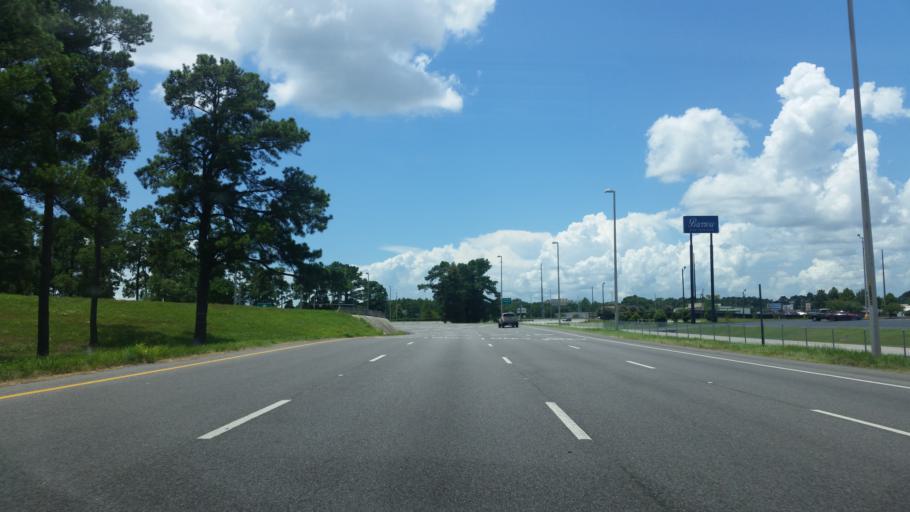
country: US
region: Alabama
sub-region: Mobile County
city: Tillmans Corner
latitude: 30.6534
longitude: -88.1241
